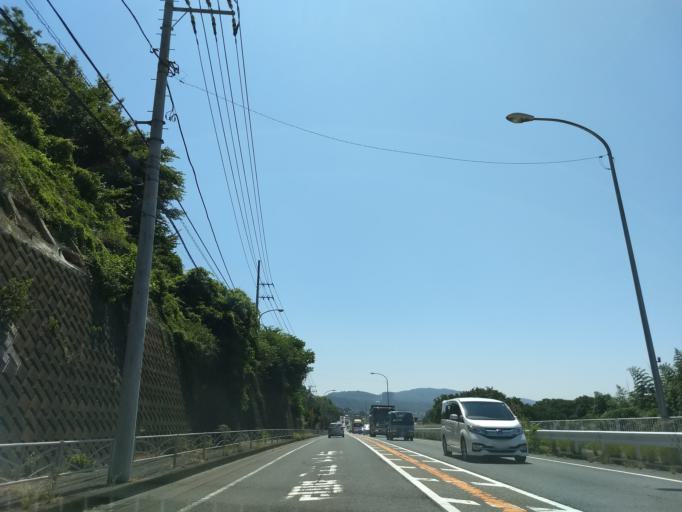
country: JP
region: Kanagawa
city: Odawara
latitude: 35.3532
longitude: 139.1185
